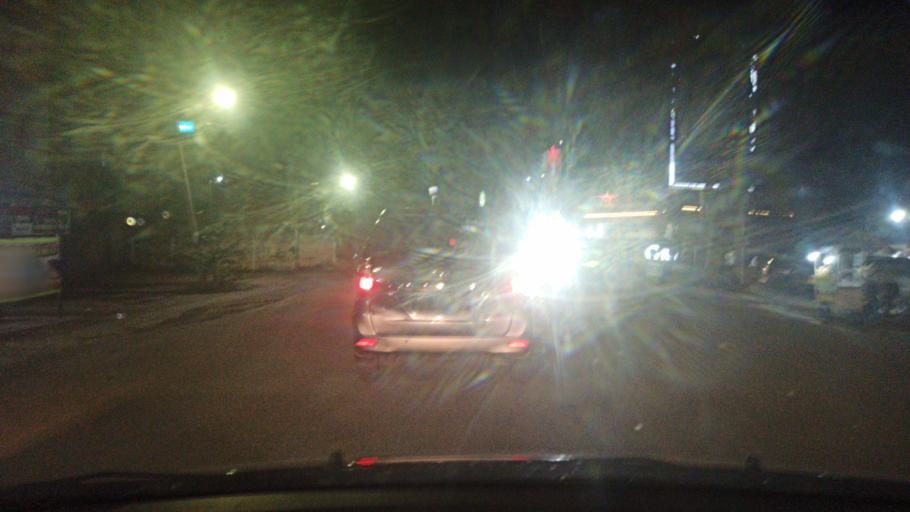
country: ID
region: South Sumatra
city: Plaju
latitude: -2.9469
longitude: 104.7854
